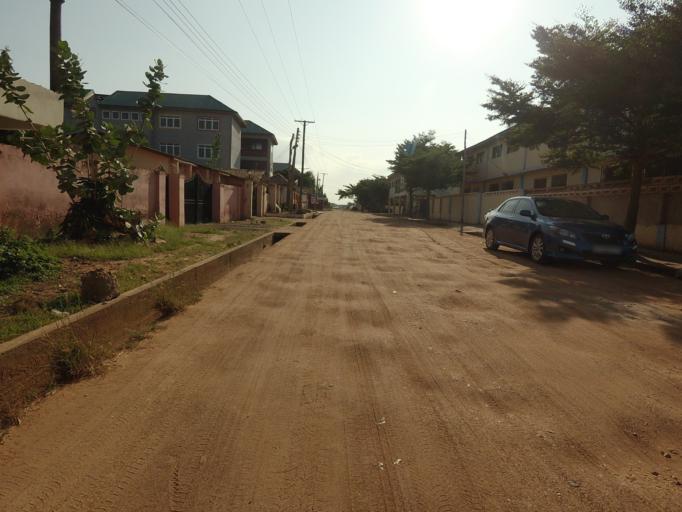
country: GH
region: Greater Accra
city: Nungua
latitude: 5.6363
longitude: -0.0868
